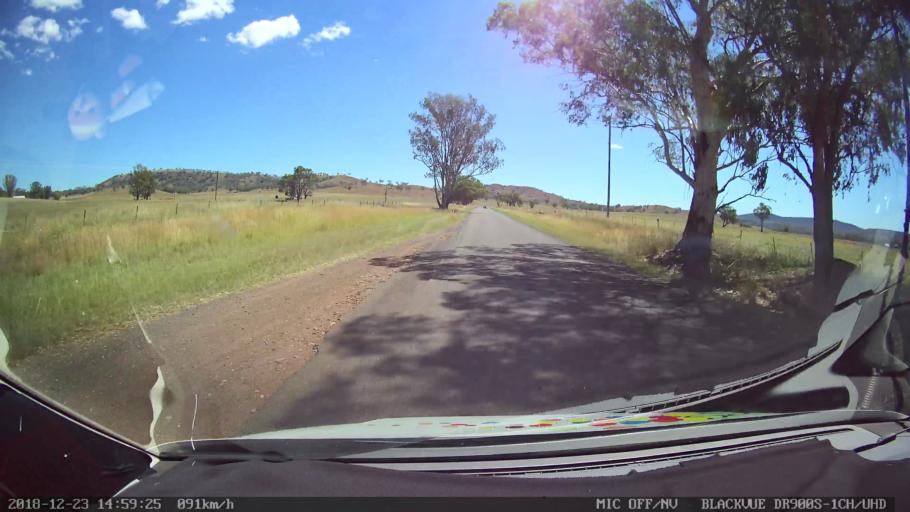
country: AU
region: New South Wales
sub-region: Tamworth Municipality
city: Manilla
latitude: -30.7237
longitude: 150.8008
